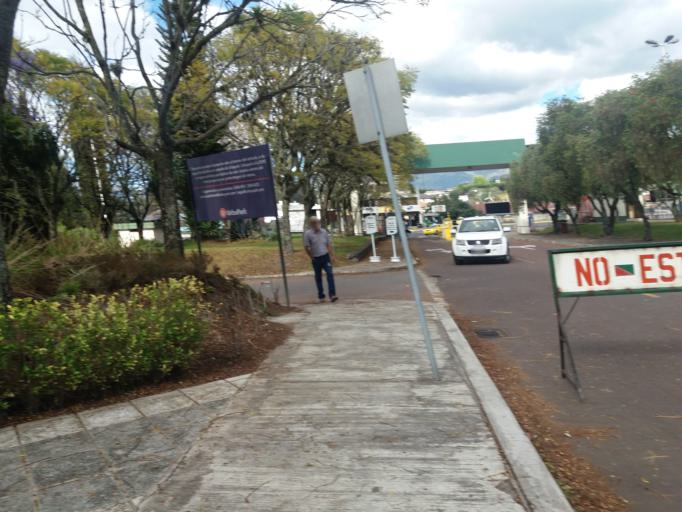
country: EC
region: Pichincha
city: Sangolqui
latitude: -0.3146
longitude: -78.4428
